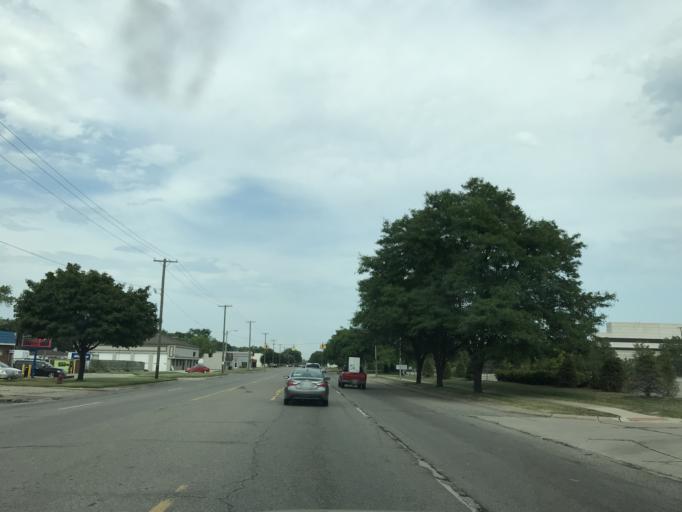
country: US
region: Michigan
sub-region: Wayne County
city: Allen Park
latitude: 42.2695
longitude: -83.2461
